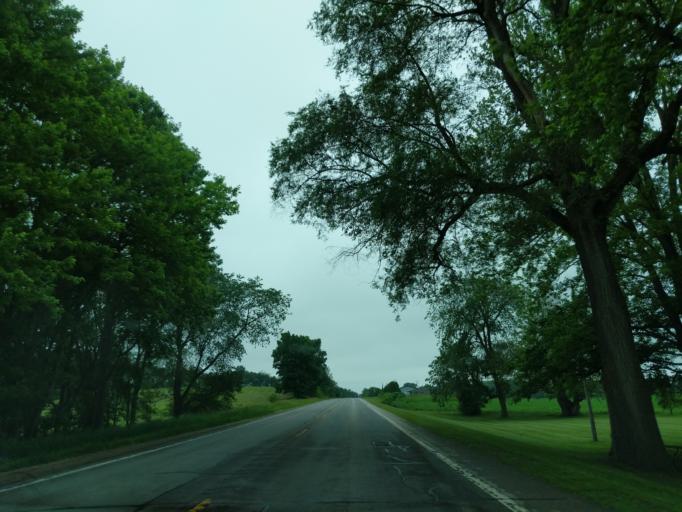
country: US
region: Michigan
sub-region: Hillsdale County
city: Litchfield
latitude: 42.0662
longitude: -84.7875
